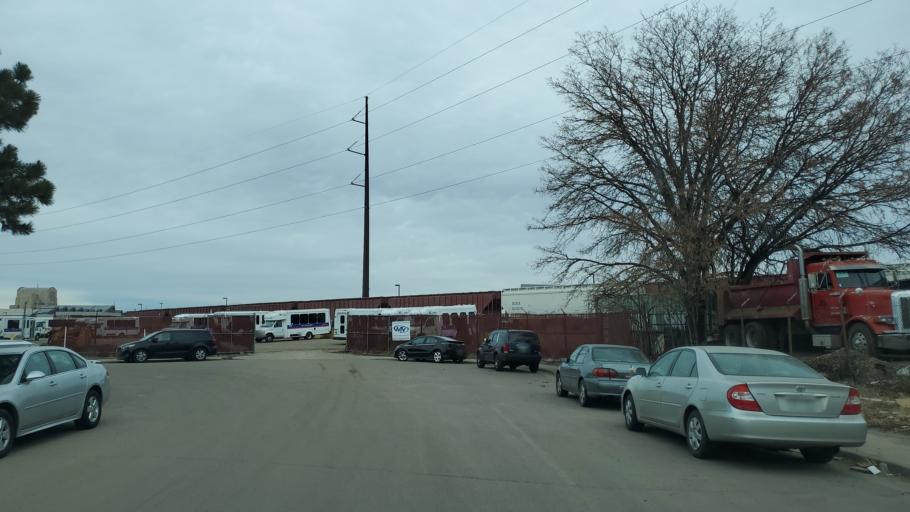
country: US
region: Colorado
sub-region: Denver County
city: Denver
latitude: 39.7153
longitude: -105.0062
